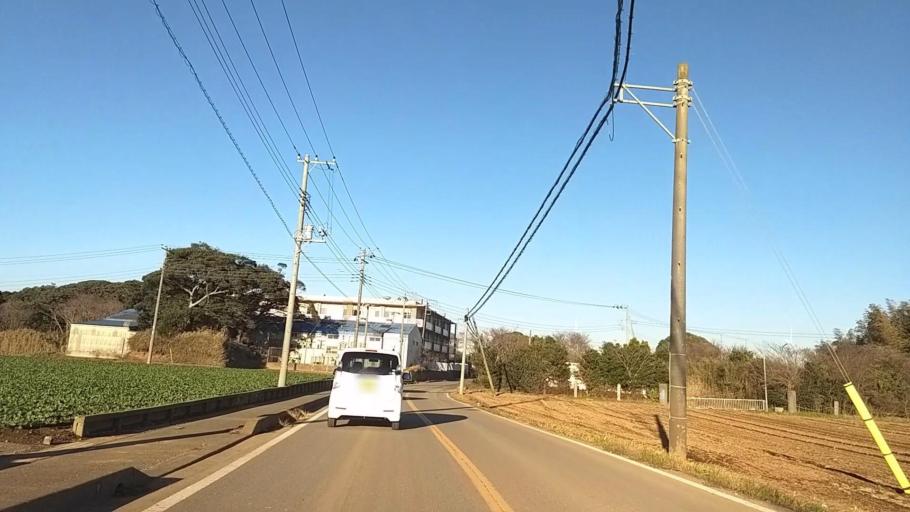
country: JP
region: Chiba
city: Hasaki
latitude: 35.7587
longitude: 140.7474
